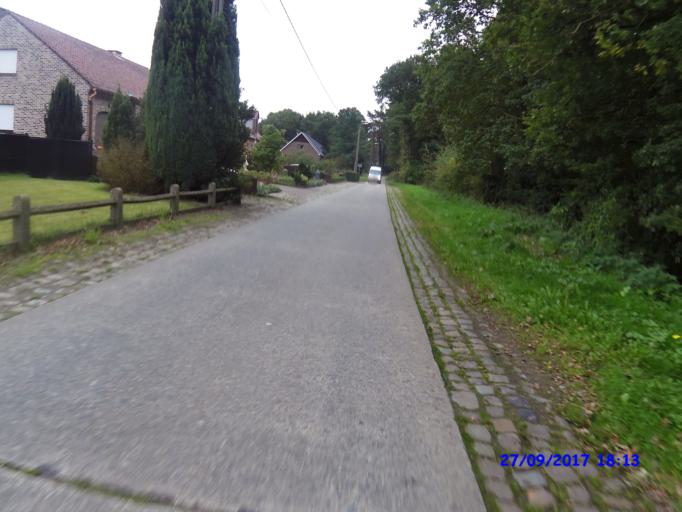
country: BE
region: Flanders
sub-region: Provincie Vlaams-Brabant
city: Begijnendijk
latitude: 50.9947
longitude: 4.8051
